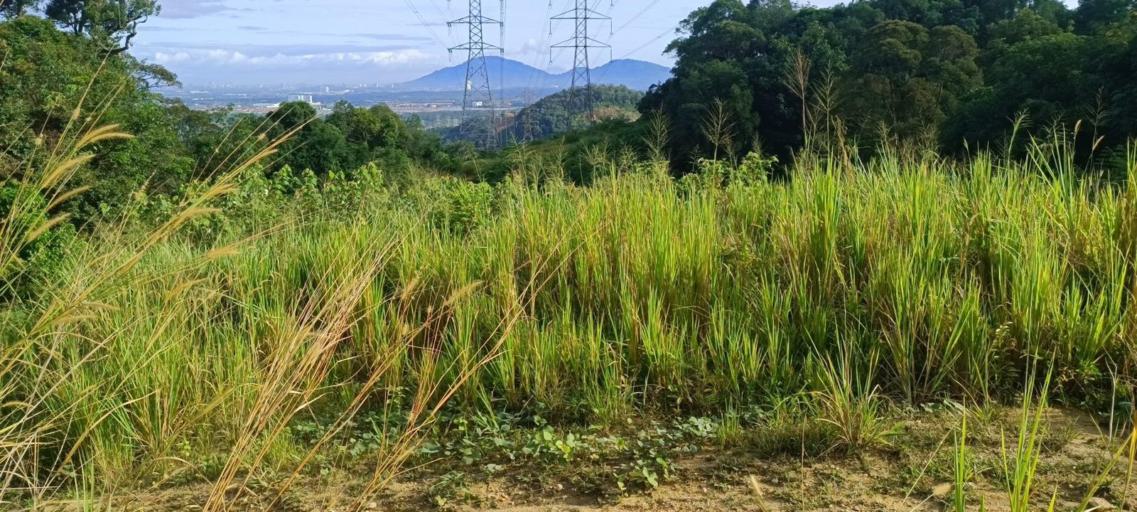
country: MY
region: Penang
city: Nibong Tebal
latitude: 5.2323
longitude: 100.5137
